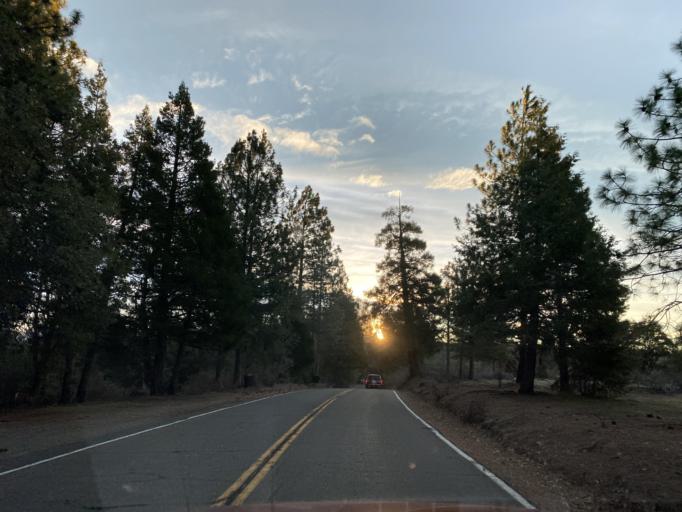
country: US
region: California
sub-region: Amador County
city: Pine Grove
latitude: 38.5003
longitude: -120.6414
